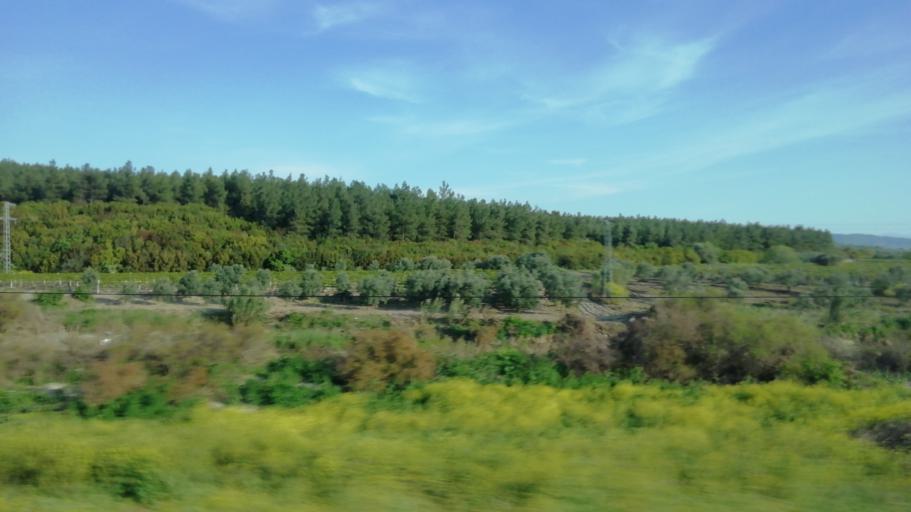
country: TR
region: Manisa
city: Halitpasa
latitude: 38.7884
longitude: 27.6746
